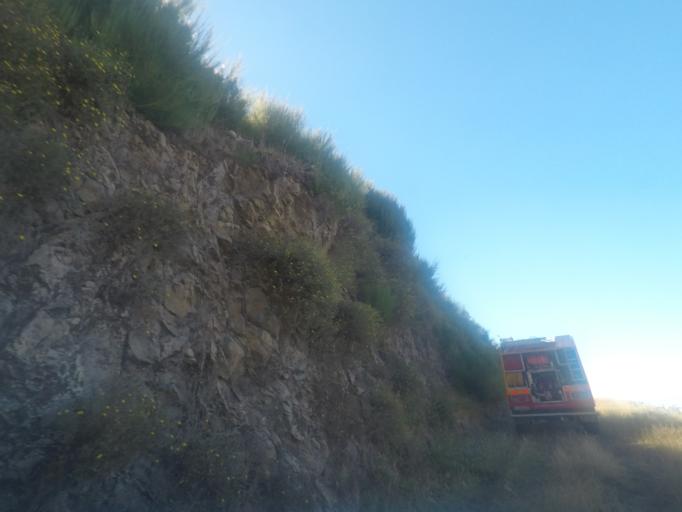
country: PT
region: Madeira
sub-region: Funchal
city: Nossa Senhora do Monte
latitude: 32.7069
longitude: -16.9168
